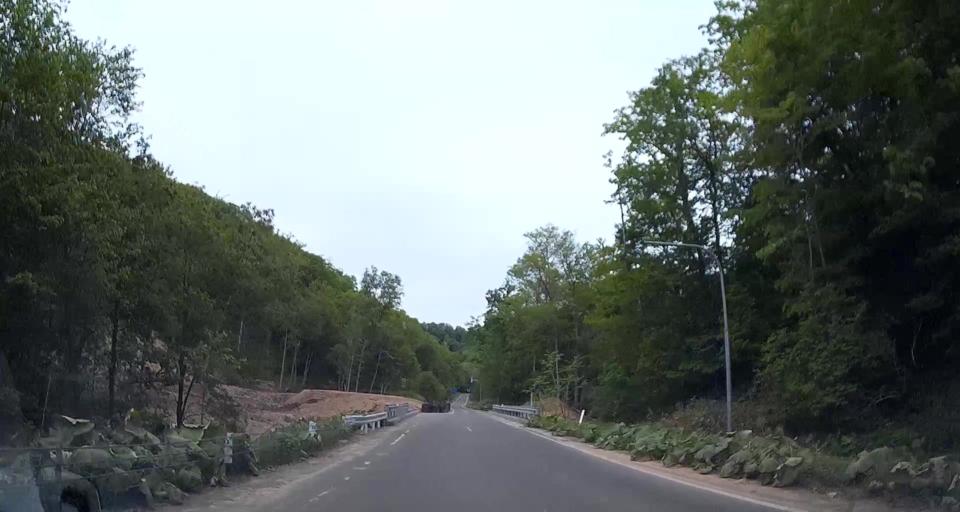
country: JP
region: Hokkaido
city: Chitose
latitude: 42.7892
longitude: 142.0506
